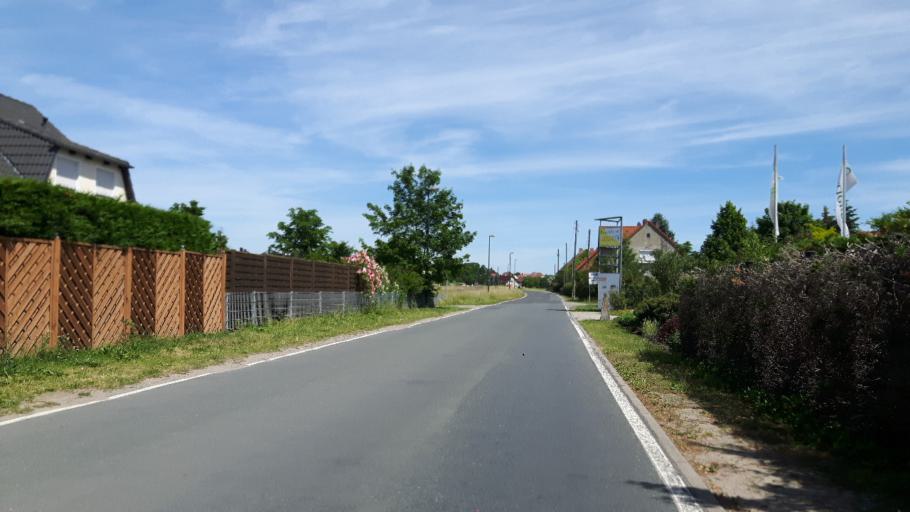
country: DE
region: Saxony-Anhalt
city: Wittenburg
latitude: 51.8953
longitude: 12.6419
